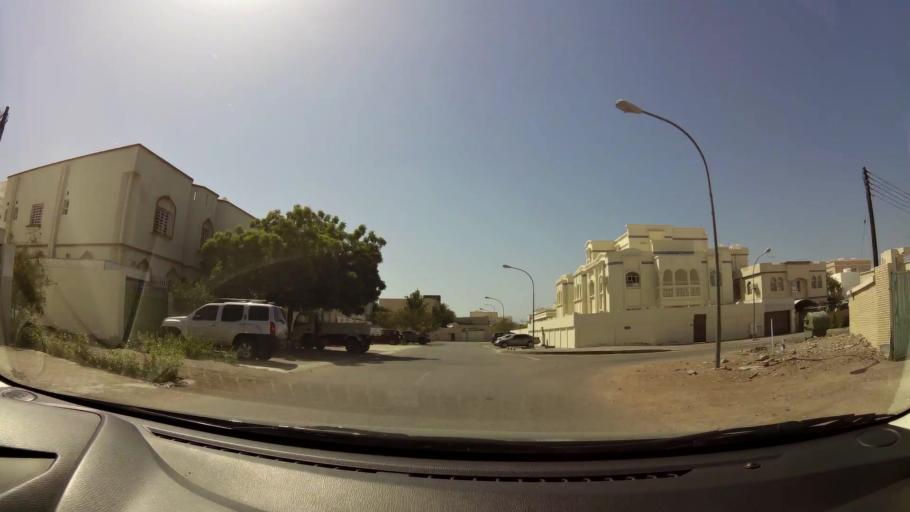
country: OM
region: Muhafazat Masqat
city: As Sib al Jadidah
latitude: 23.6343
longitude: 58.2153
